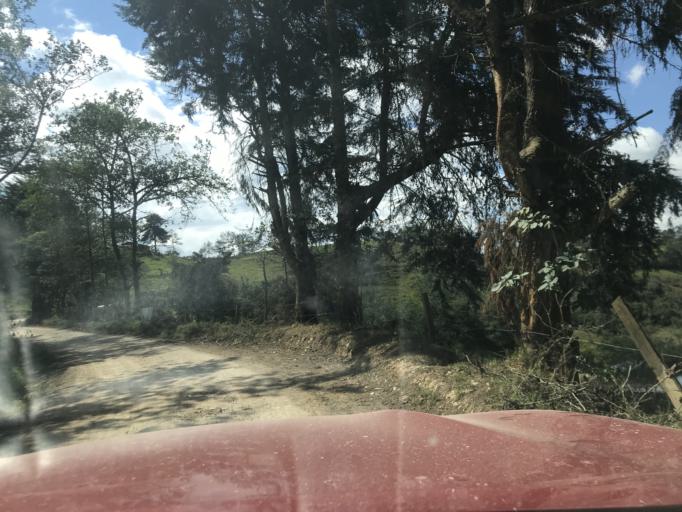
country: PE
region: Cajamarca
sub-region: Provincia de Chota
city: Querocoto
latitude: -6.3451
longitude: -79.0469
